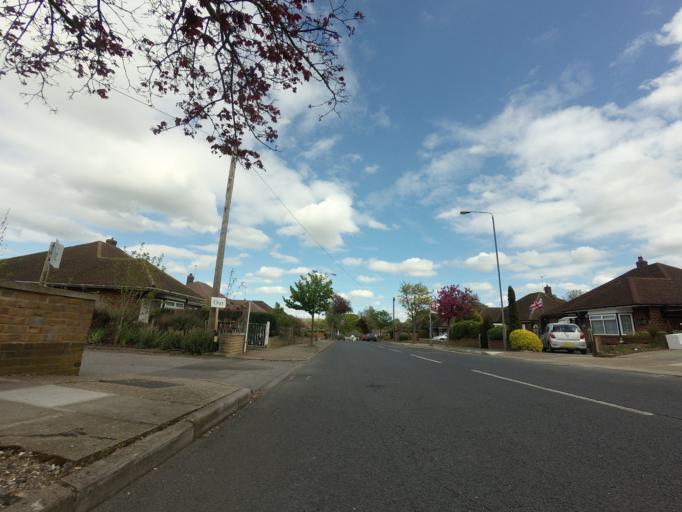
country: GB
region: England
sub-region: Greater London
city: Orpington
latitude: 51.3697
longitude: 0.1206
